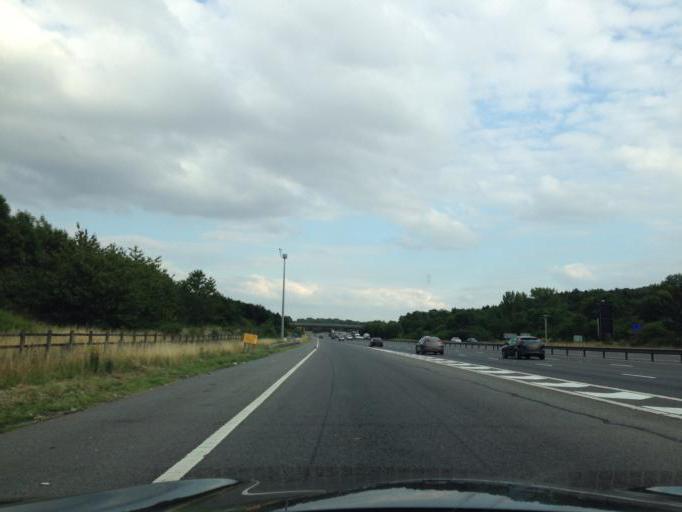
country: GB
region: England
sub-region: Warwickshire
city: Harbury
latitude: 52.2175
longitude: -1.5015
